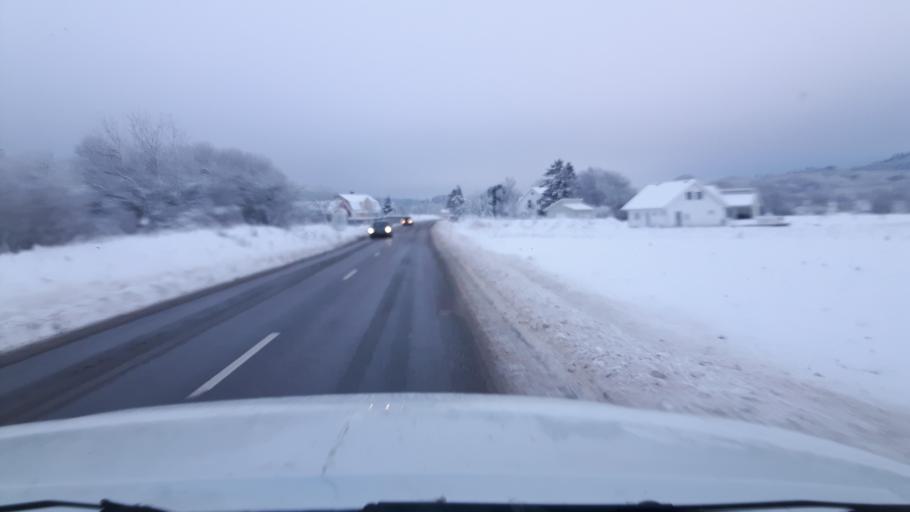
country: SE
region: Halland
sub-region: Kungsbacka Kommun
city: Fjaeras kyrkby
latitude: 57.4257
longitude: 12.1950
